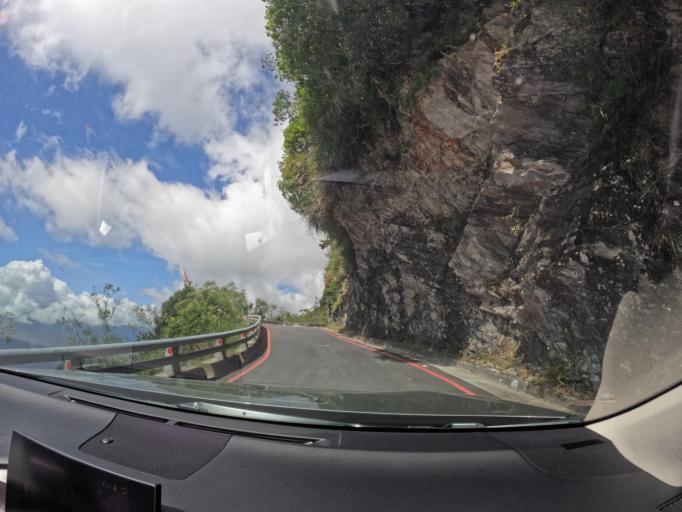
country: TW
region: Taiwan
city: Yujing
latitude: 23.2619
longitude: 120.9483
